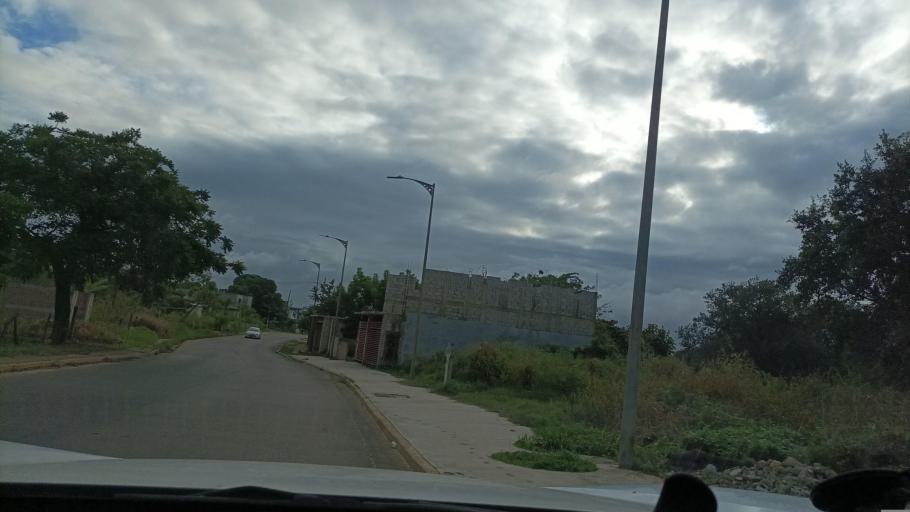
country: MX
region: Veracruz
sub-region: Cosoleacaque
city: Hermenegildo J. Aldana
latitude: 17.9973
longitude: -94.6109
